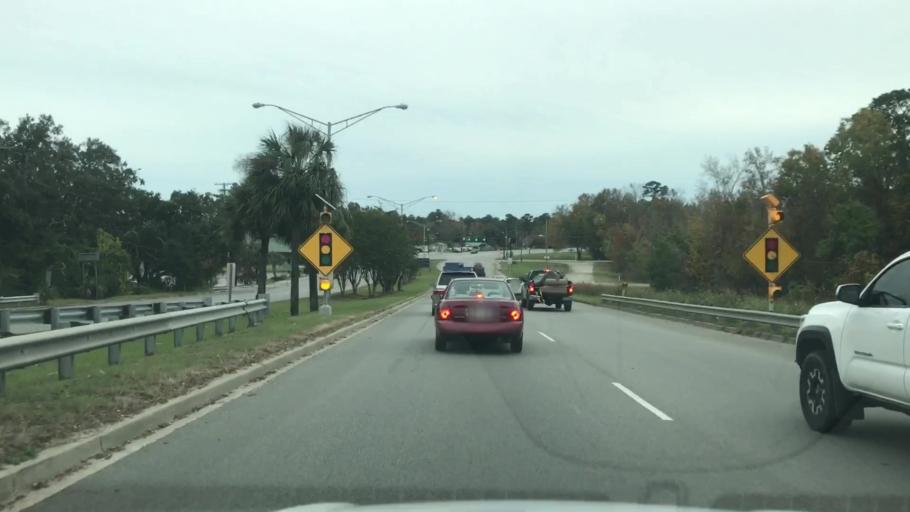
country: US
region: South Carolina
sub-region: Georgetown County
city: Georgetown
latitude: 33.3545
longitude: -79.2934
